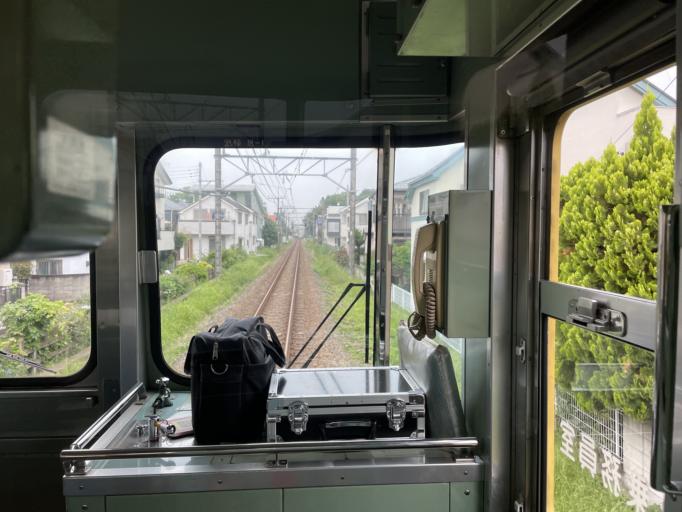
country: JP
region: Tokyo
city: Kokubunji
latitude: 35.7195
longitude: 139.4605
